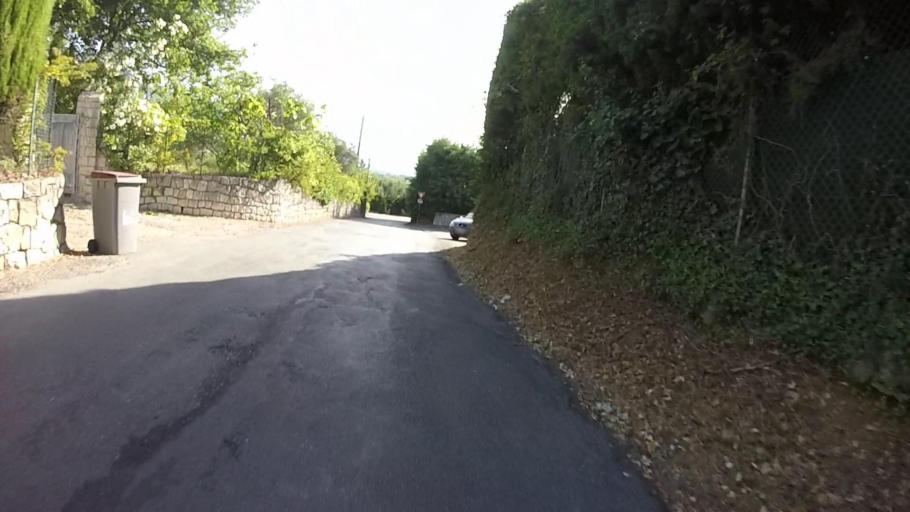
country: FR
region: Provence-Alpes-Cote d'Azur
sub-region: Departement des Alpes-Maritimes
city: Chateauneuf-Grasse
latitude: 43.6711
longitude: 6.9992
